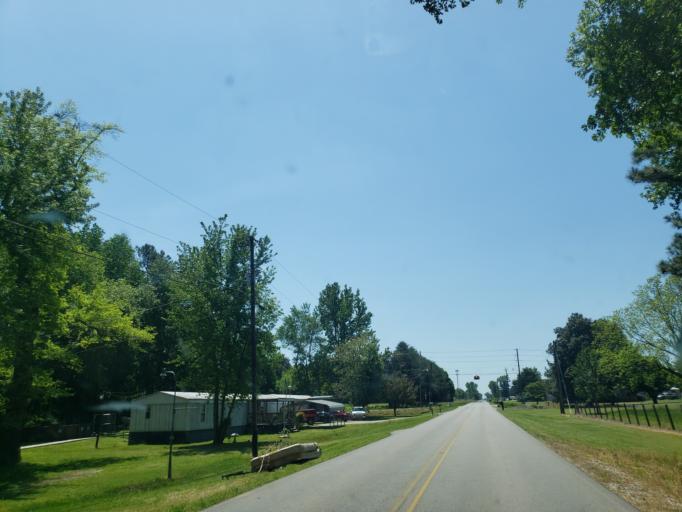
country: US
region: Alabama
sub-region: Madison County
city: Harvest
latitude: 34.8956
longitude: -86.7345
